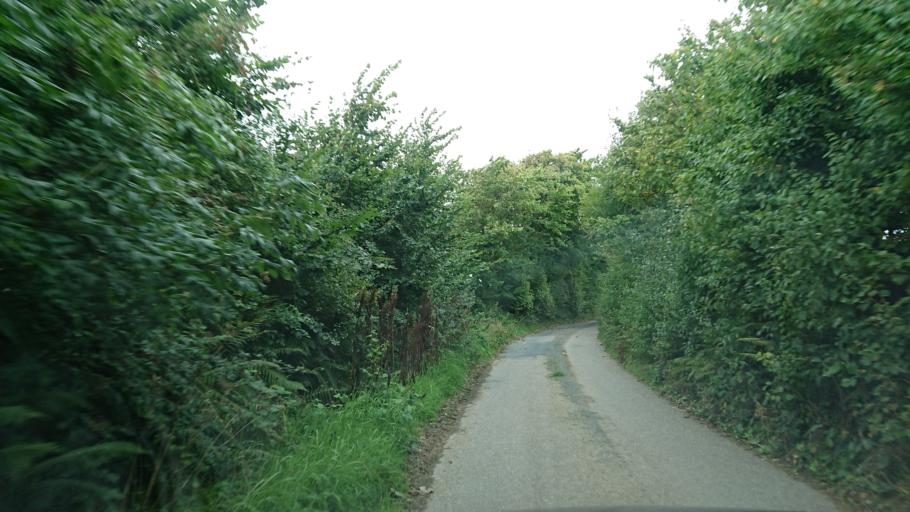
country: IE
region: Munster
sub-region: Waterford
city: Dunmore East
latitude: 52.2096
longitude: -7.0430
